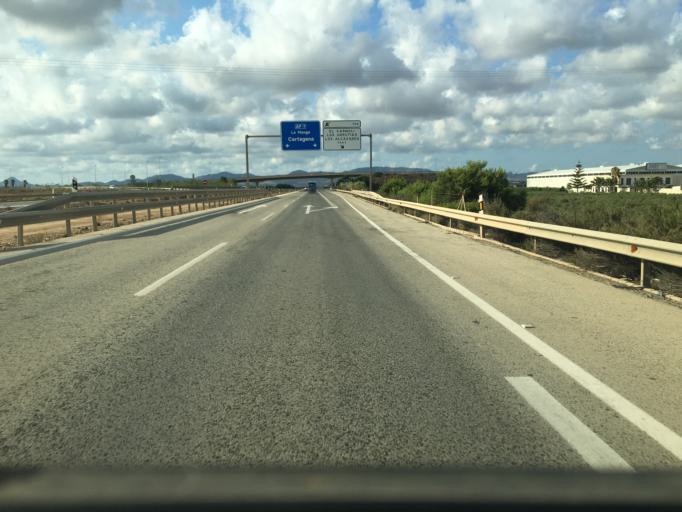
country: ES
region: Murcia
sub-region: Murcia
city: Los Alcazares
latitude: 37.7075
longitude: -0.8663
